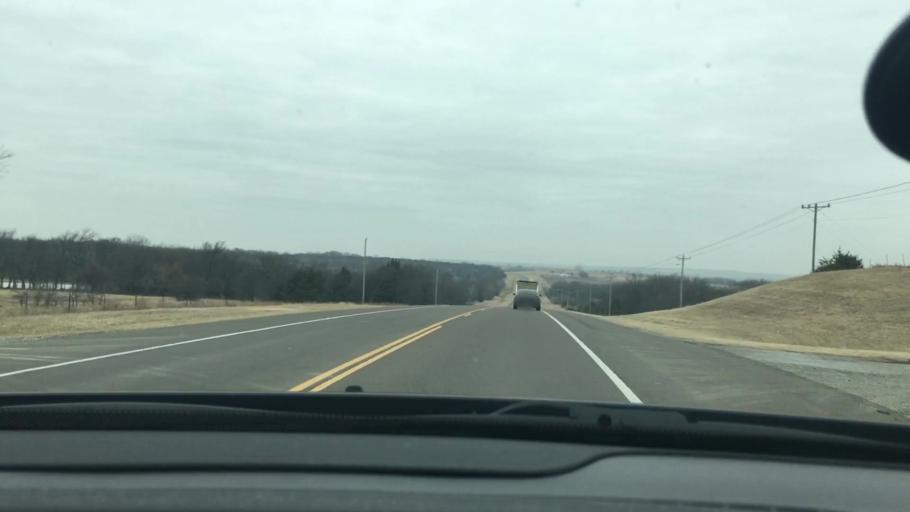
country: US
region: Oklahoma
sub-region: Murray County
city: Davis
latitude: 34.5117
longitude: -97.1982
